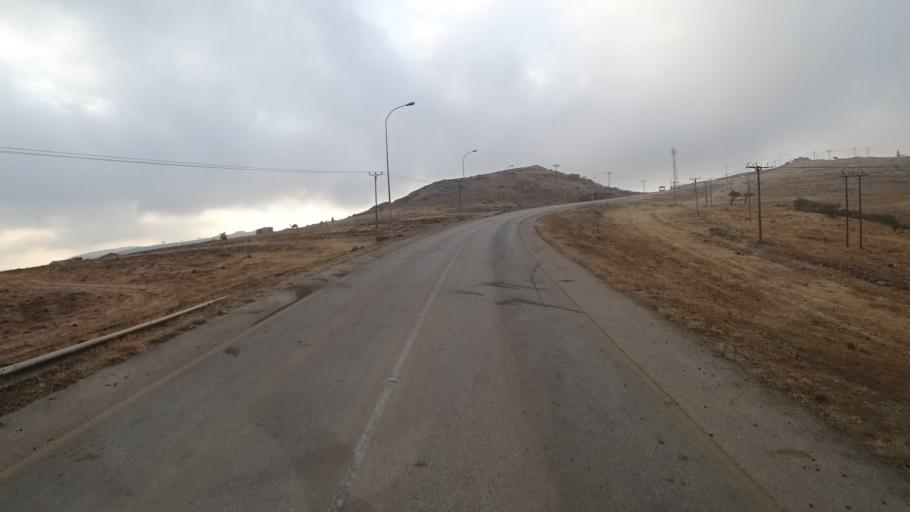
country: OM
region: Zufar
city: Salalah
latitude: 17.1197
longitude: 53.9790
